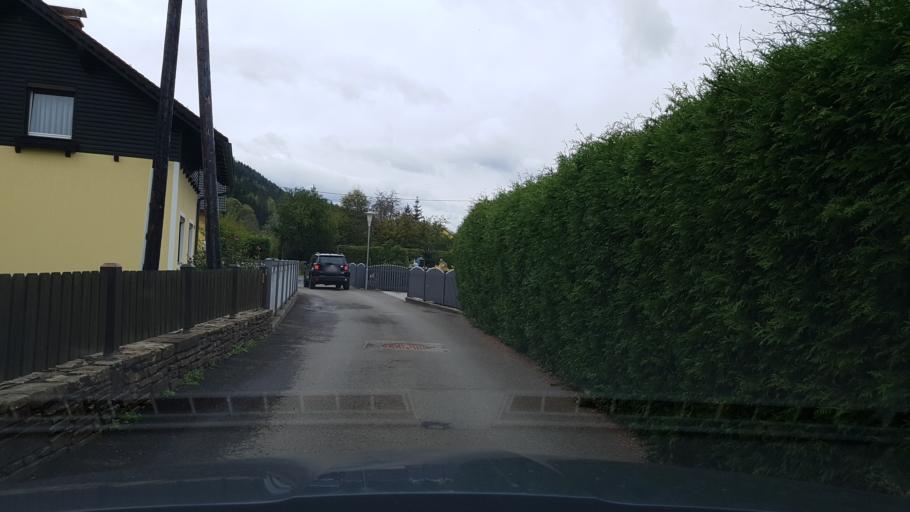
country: AT
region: Styria
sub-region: Politischer Bezirk Bruck-Muerzzuschlag
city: Sankt Marein im Muerztal
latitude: 47.4666
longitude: 15.3768
